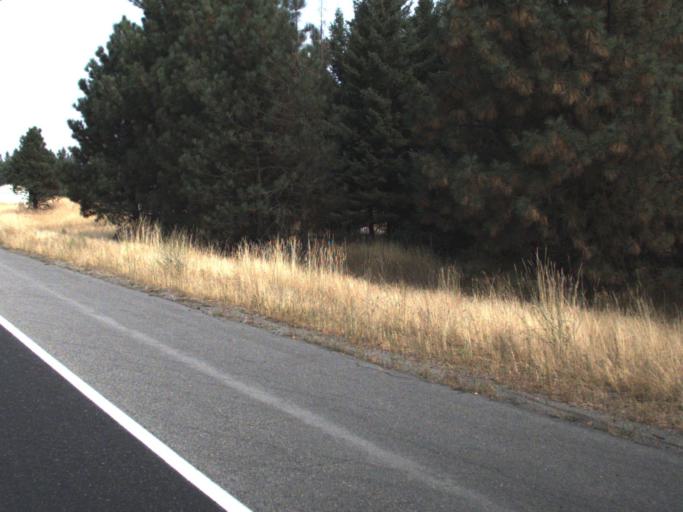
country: US
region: Washington
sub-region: Spokane County
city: Fairwood
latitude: 47.8218
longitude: -117.4131
